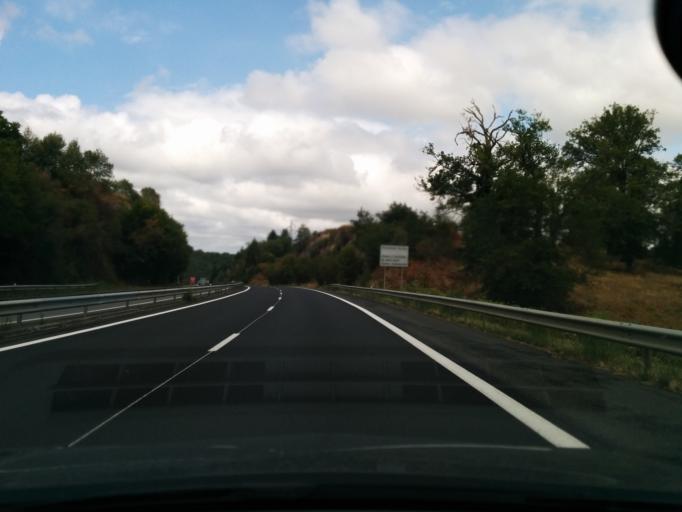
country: FR
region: Limousin
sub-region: Departement de la Correze
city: Brive-la-Gaillarde
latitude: 45.1215
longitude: 1.5001
